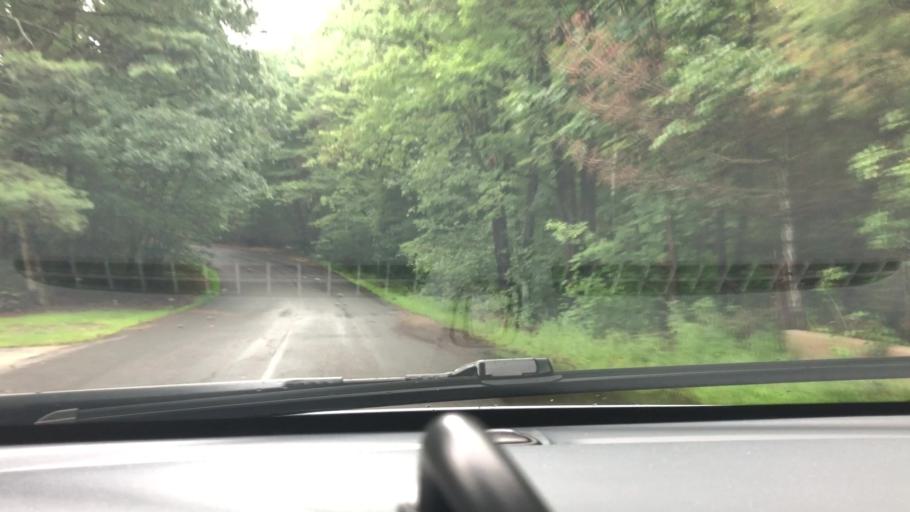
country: US
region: New Hampshire
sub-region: Hillsborough County
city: Pinardville
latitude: 43.0007
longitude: -71.4983
